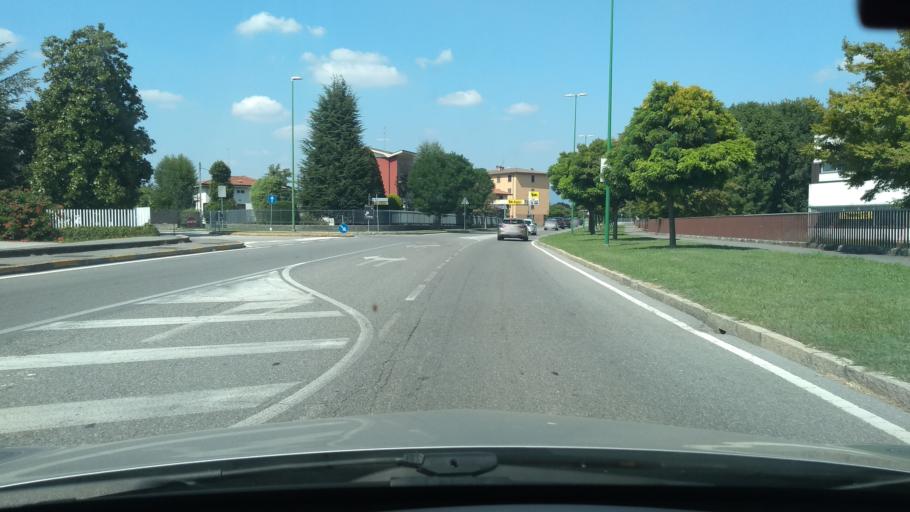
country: IT
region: Lombardy
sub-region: Provincia di Bergamo
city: Ghisalba
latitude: 45.5963
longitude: 9.7566
